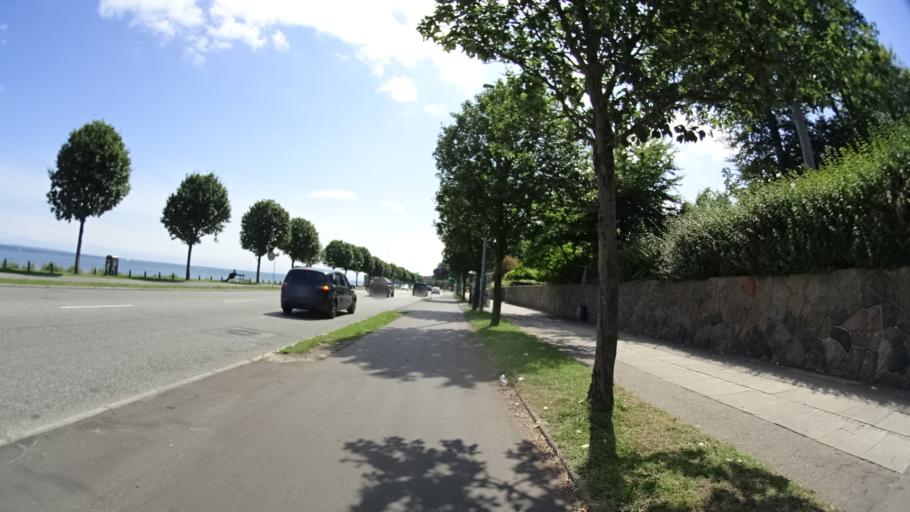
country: DK
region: Central Jutland
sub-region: Arhus Kommune
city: Arhus
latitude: 56.1358
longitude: 10.2084
